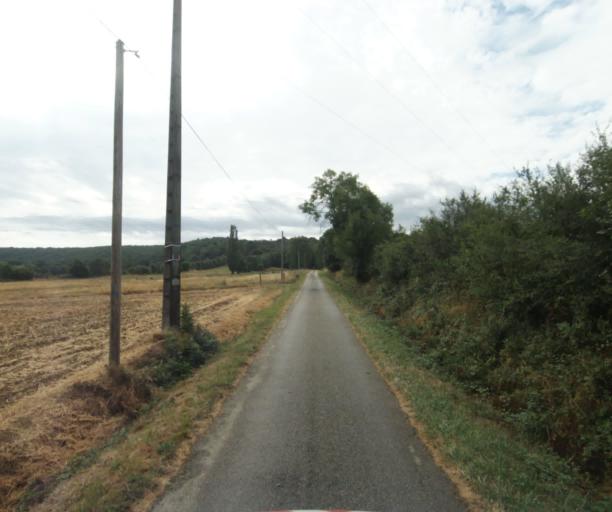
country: FR
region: Midi-Pyrenees
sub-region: Departement de la Haute-Garonne
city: Revel
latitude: 43.4160
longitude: 1.9720
